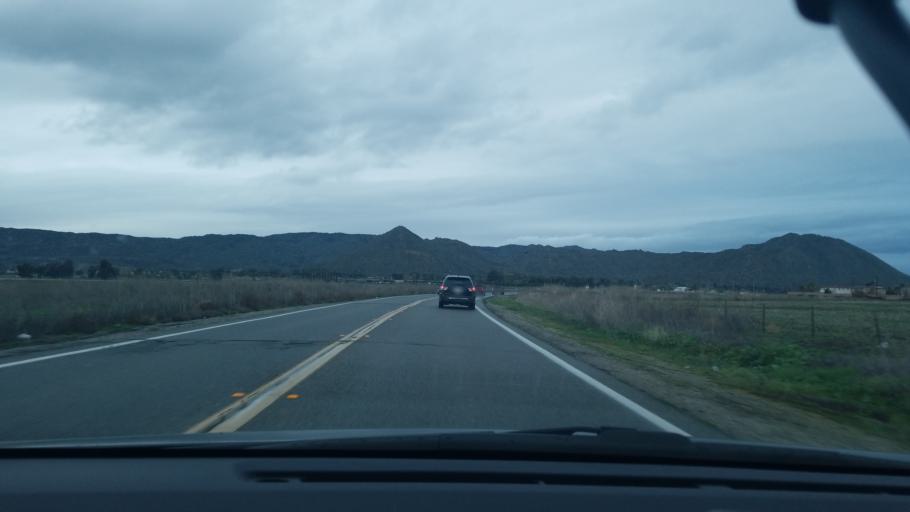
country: US
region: California
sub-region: Riverside County
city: Green Acres
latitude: 33.7476
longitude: -117.0345
